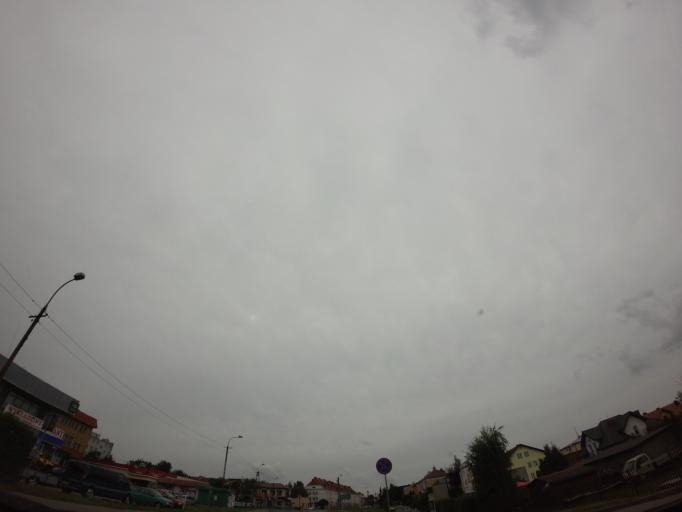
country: PL
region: Masovian Voivodeship
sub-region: Powiat ciechanowski
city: Ciechanow
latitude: 52.8815
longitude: 20.6254
